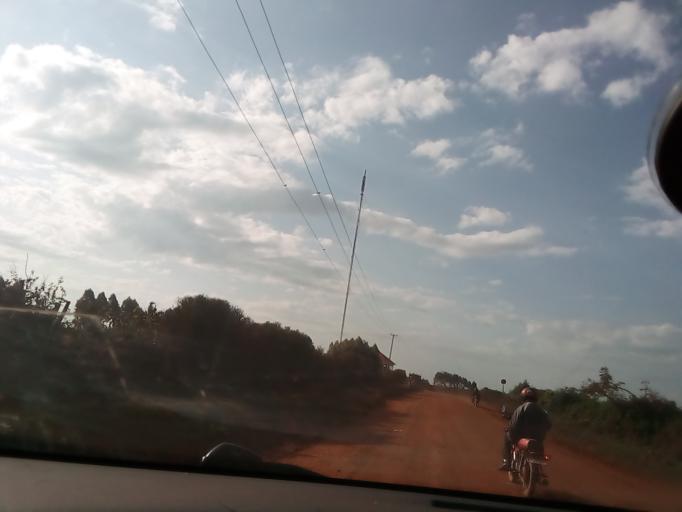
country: UG
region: Central Region
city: Masaka
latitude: -0.3609
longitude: 31.7464
